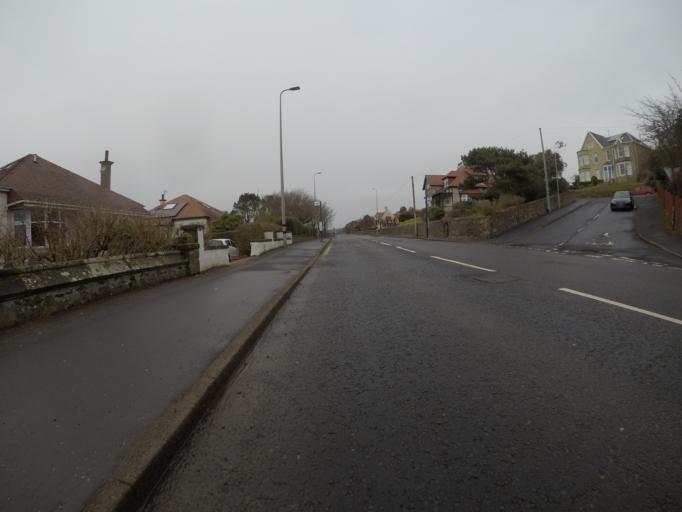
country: GB
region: Scotland
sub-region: North Ayrshire
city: West Kilbride
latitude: 55.6917
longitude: -4.8657
